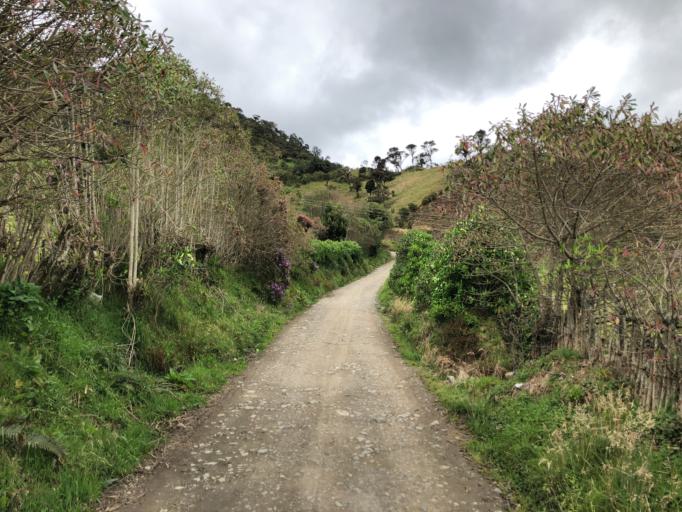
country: CO
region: Cauca
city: Totoro
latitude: 2.5019
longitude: -76.3592
